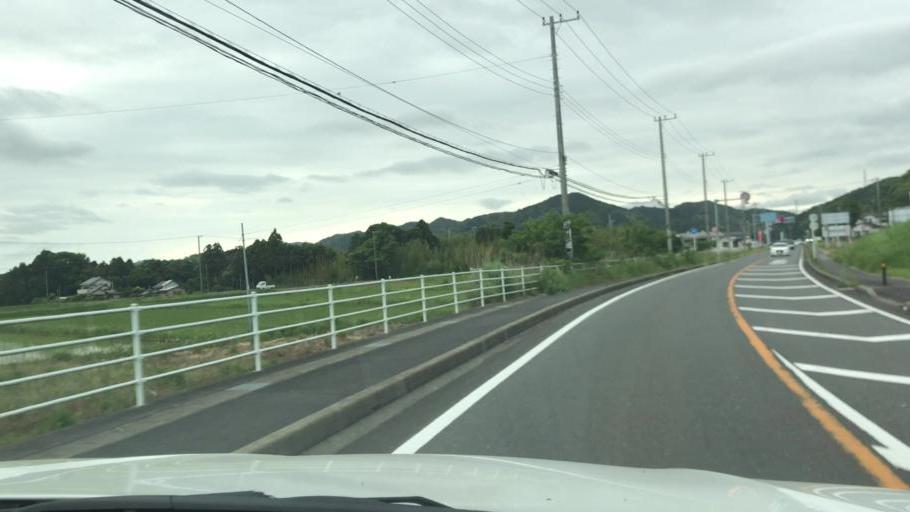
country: JP
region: Chiba
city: Kawaguchi
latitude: 35.1230
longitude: 140.0820
